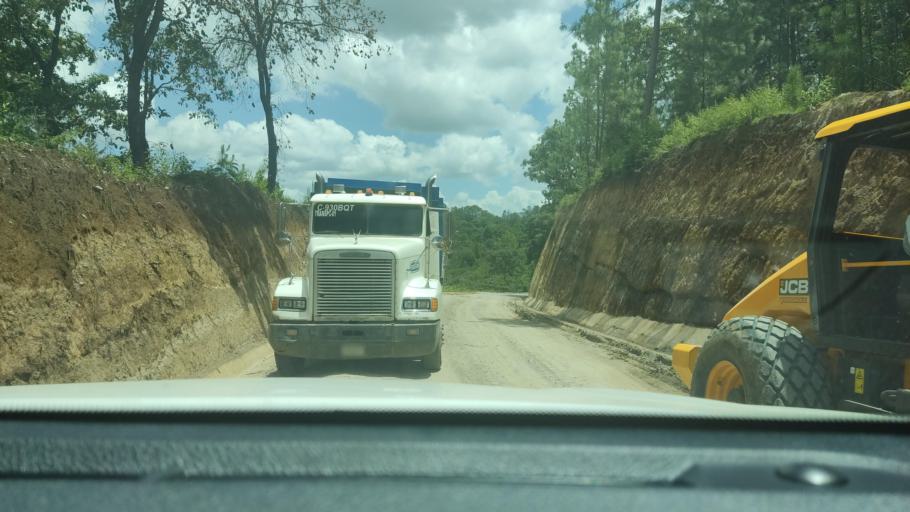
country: GT
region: Chimaltenango
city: San Martin Jilotepeque
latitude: 14.7950
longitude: -90.8118
